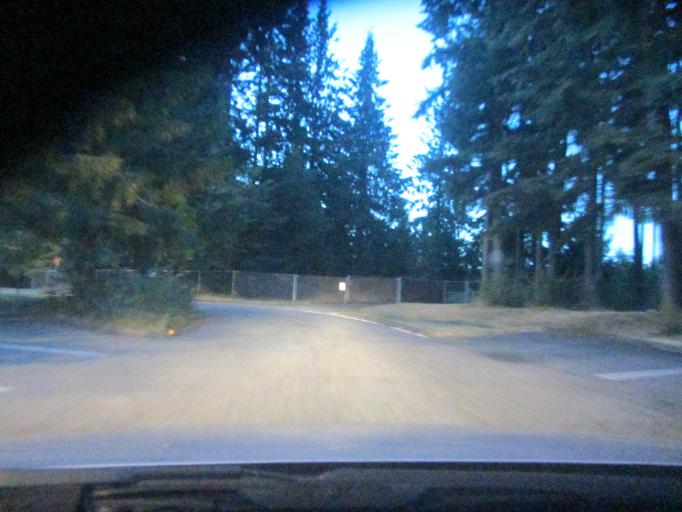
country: US
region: Washington
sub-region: Snohomish County
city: Smokey Point
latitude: 48.1696
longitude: -122.1888
